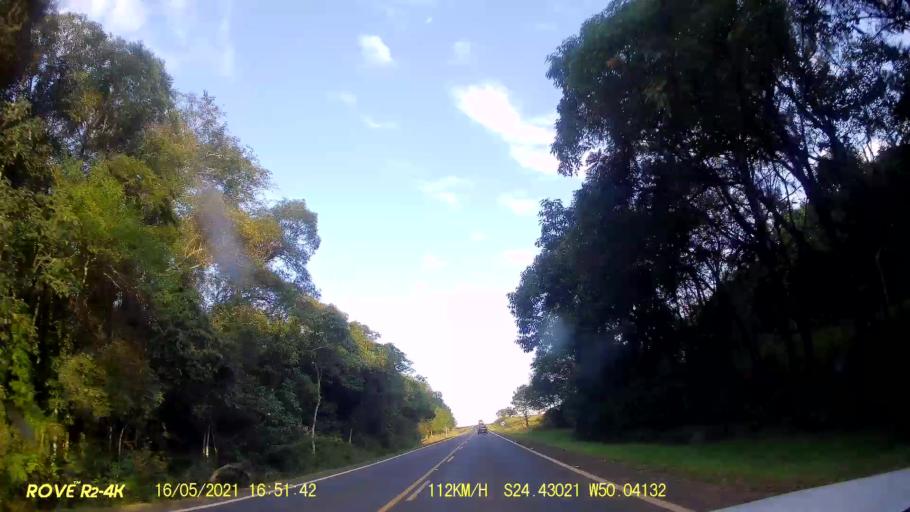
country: BR
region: Parana
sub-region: Pirai Do Sul
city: Pirai do Sul
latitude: -24.4303
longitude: -50.0413
